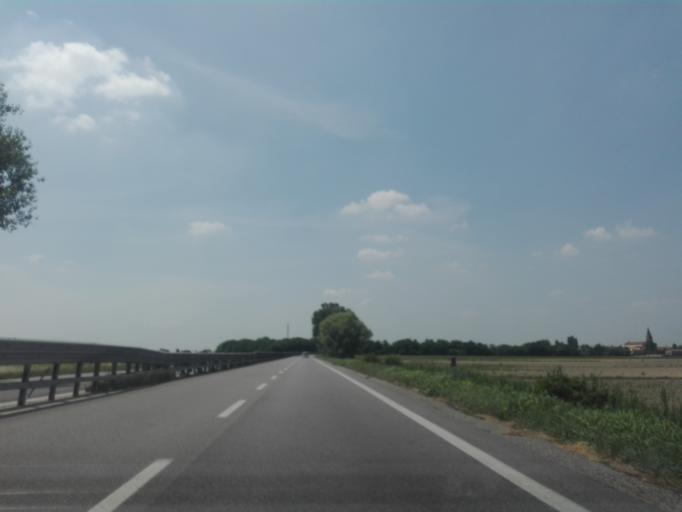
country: IT
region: Veneto
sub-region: Provincia di Rovigo
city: San Bellino
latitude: 45.0243
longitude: 11.5967
